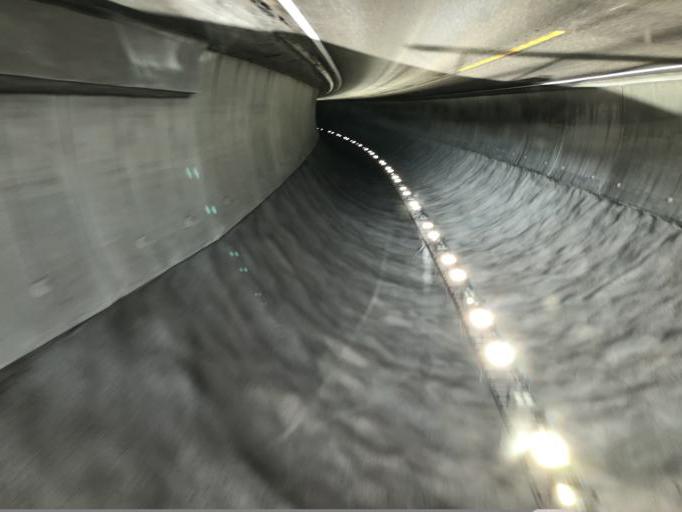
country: NO
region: Nordland
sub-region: Narvik
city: Narvik
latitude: 68.4790
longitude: 17.5004
